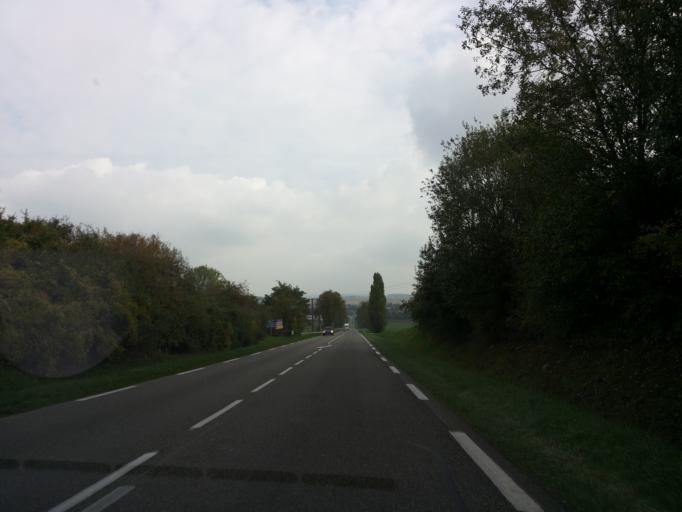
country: FR
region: Lorraine
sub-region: Departement de la Moselle
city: Solgne
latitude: 48.8911
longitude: 6.3698
